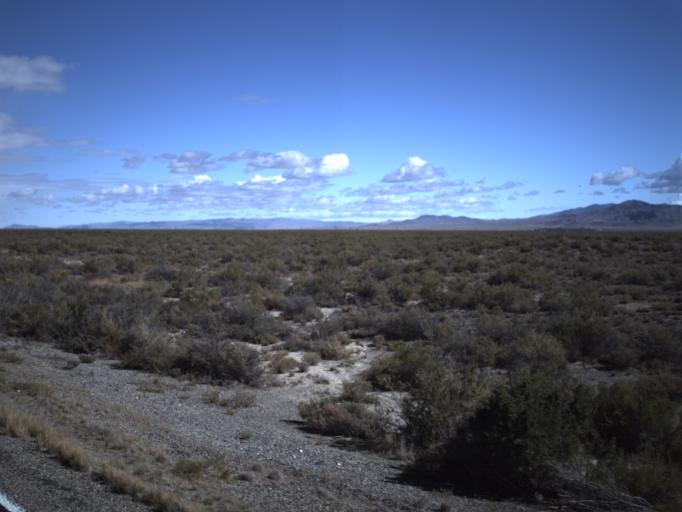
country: US
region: Nevada
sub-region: White Pine County
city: McGill
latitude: 39.0501
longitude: -114.0364
